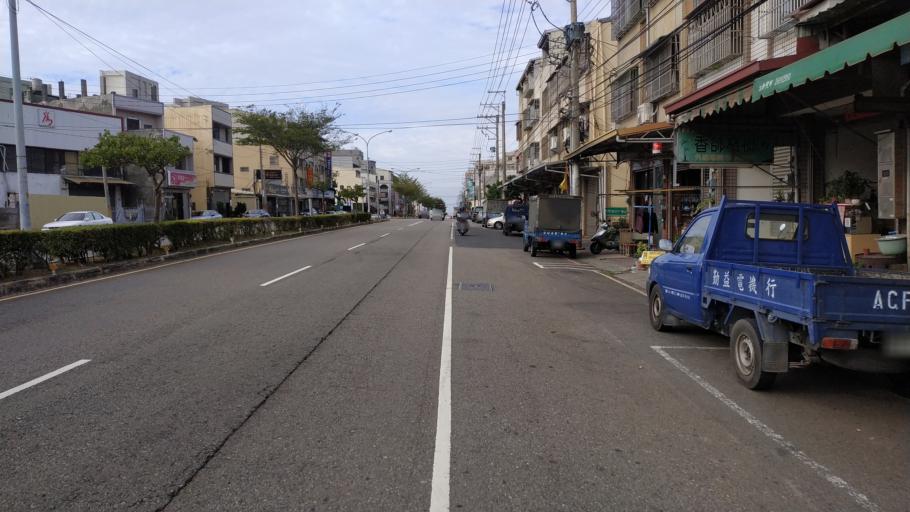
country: TW
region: Taiwan
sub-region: Taichung City
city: Taichung
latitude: 24.2273
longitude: 120.5677
